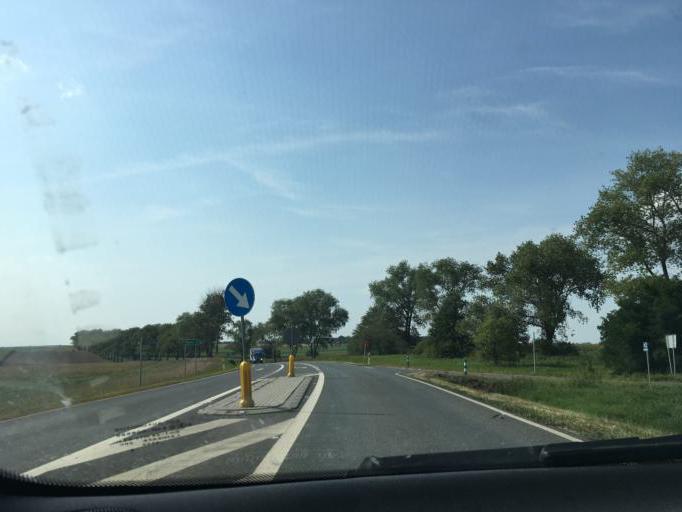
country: PL
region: Opole Voivodeship
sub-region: Powiat prudnicki
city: Laka Prudnicka
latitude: 50.4186
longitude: 17.4824
